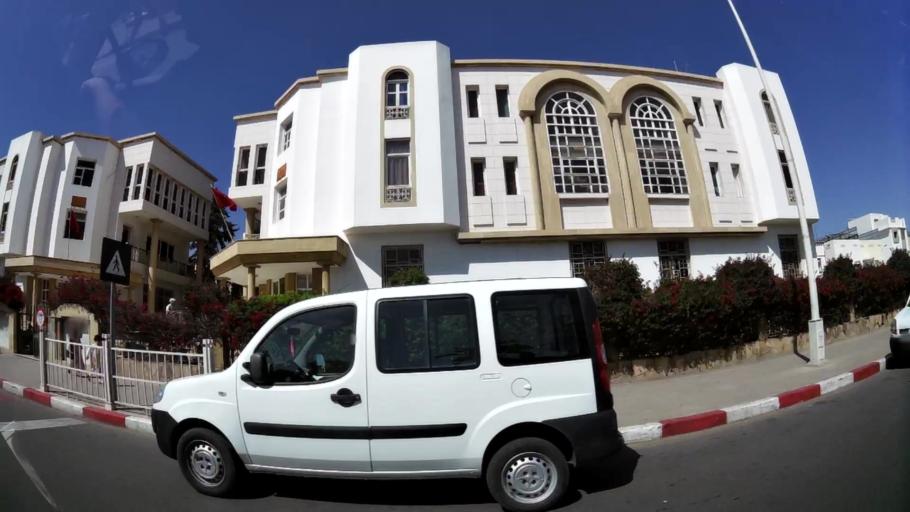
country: MA
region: Souss-Massa-Draa
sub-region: Agadir-Ida-ou-Tnan
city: Agadir
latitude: 30.4237
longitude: -9.5874
